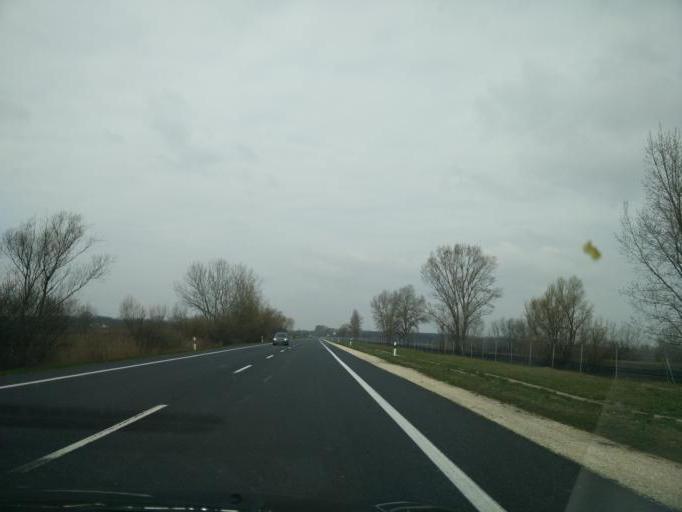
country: HU
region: Gyor-Moson-Sopron
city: Toltestava
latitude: 47.7017
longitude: 17.7674
